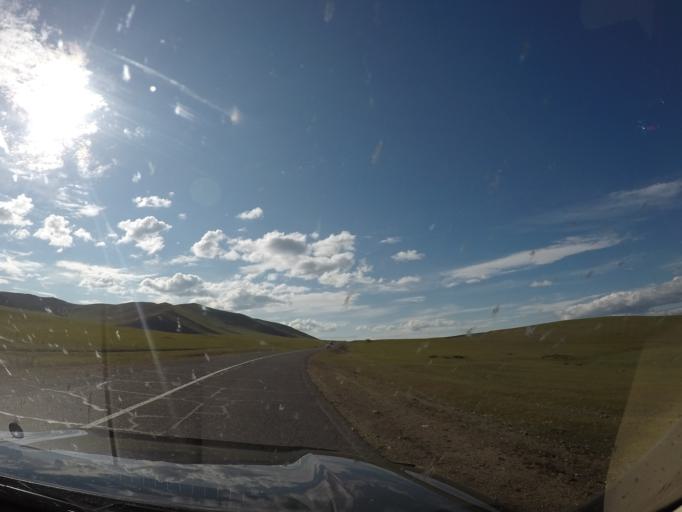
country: MN
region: Hentiy
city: Modot
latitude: 47.7459
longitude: 108.9768
